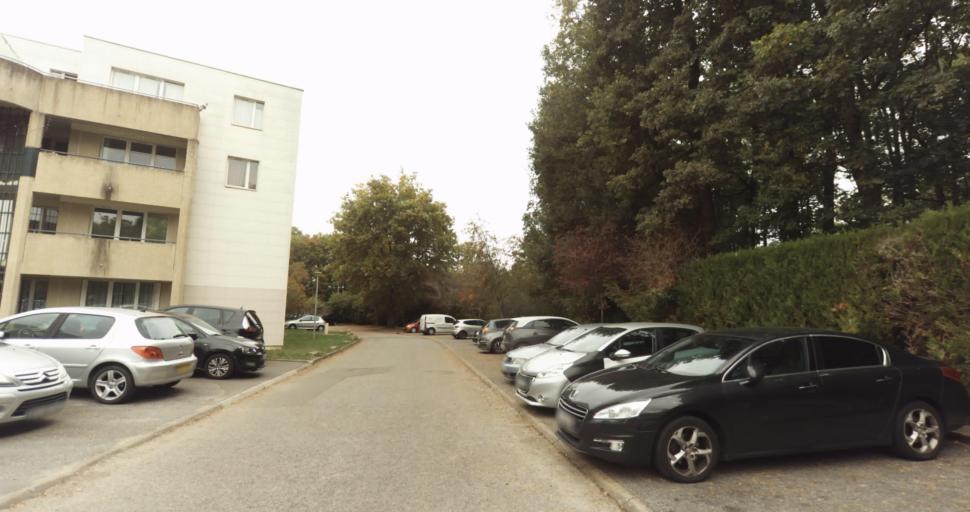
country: FR
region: Centre
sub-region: Departement d'Eure-et-Loir
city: Vernouillet
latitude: 48.7106
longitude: 1.3564
